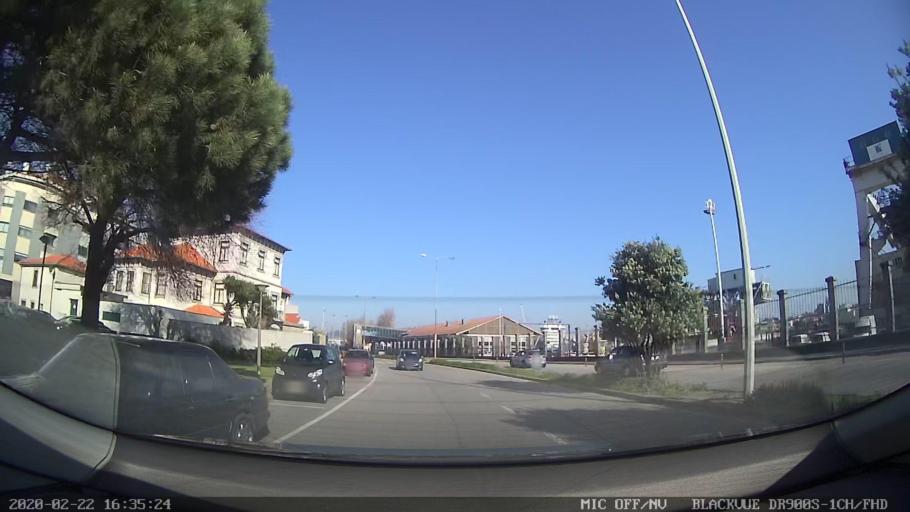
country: PT
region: Porto
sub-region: Matosinhos
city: Leca da Palmeira
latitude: 41.1869
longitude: -8.7006
